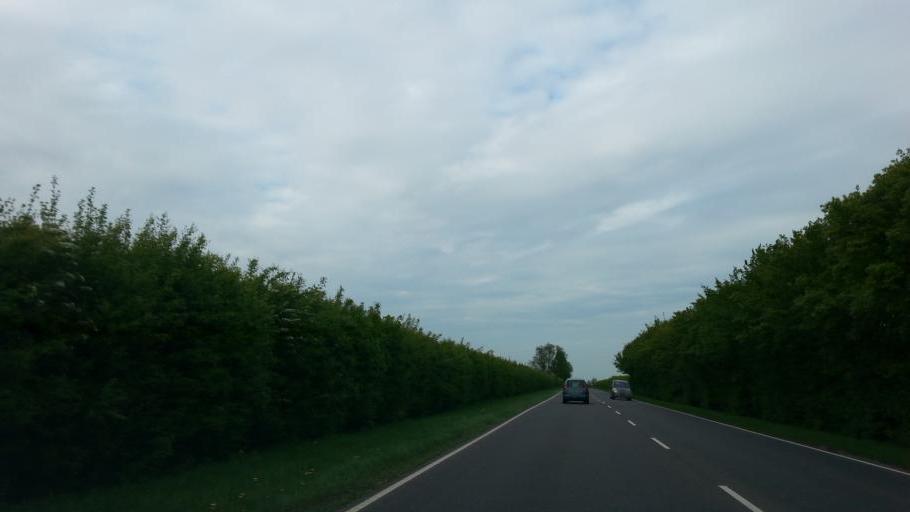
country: GB
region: England
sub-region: Cambridgeshire
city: Doddington
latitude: 52.4952
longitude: 0.0738
